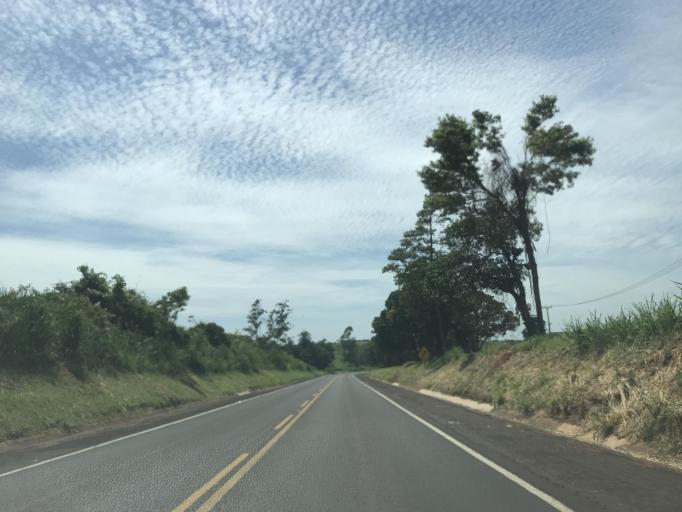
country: BR
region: Parana
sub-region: Paranavai
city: Nova Aurora
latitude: -22.9729
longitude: -52.6143
